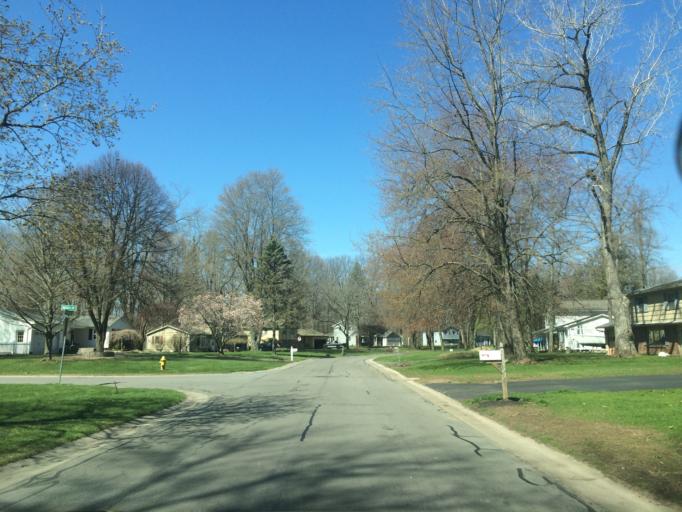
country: US
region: New York
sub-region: Monroe County
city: East Rochester
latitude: 43.0940
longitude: -77.4673
